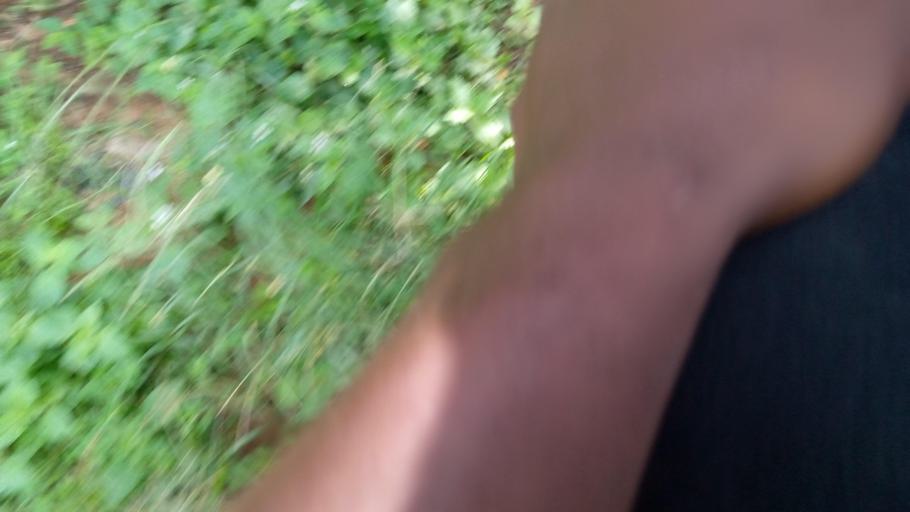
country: SL
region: Southern Province
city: Pujehun
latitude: 7.3565
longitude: -11.7258
